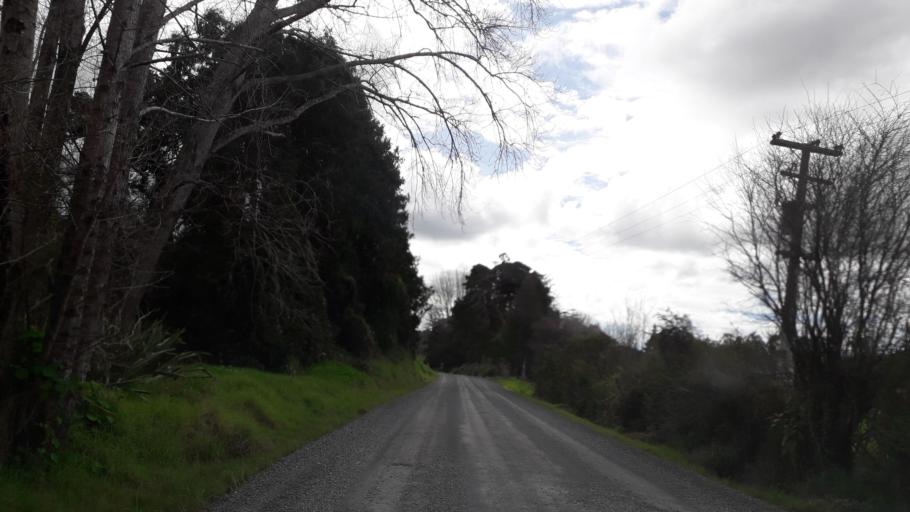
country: NZ
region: Northland
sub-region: Far North District
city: Taipa
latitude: -35.0875
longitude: 173.5119
